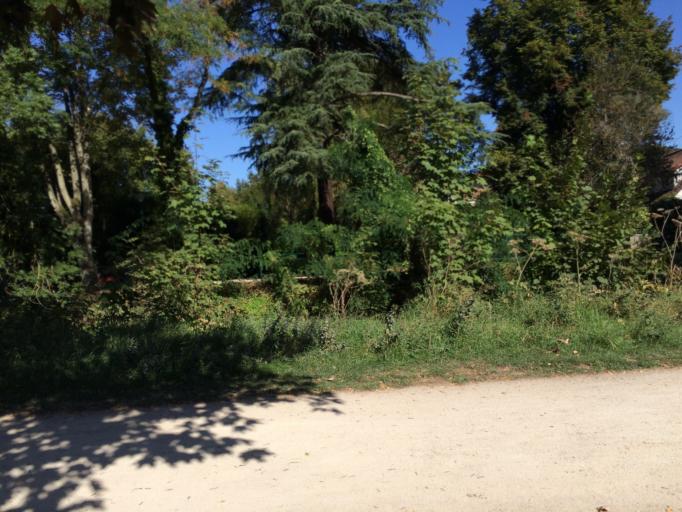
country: FR
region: Ile-de-France
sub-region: Departement de l'Essonne
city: Orsay
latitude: 48.7011
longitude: 2.1975
